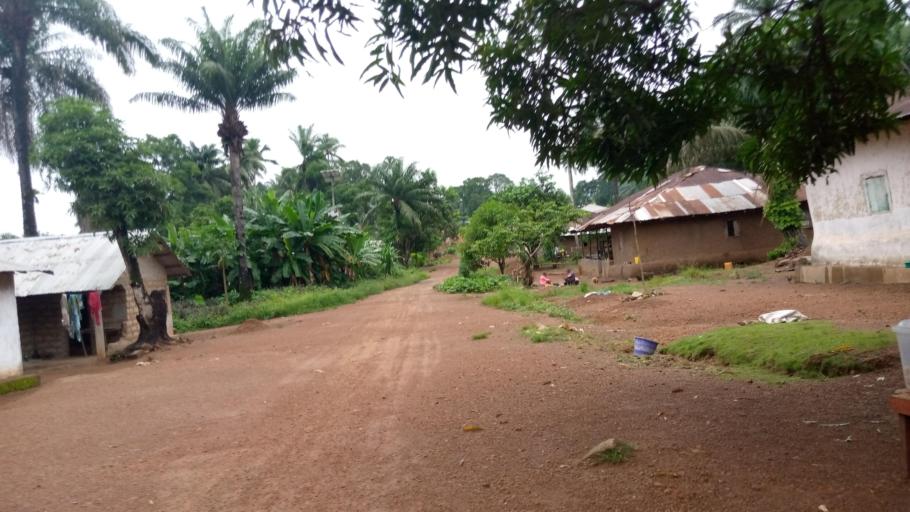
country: SL
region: Southern Province
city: Moyamba
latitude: 8.1630
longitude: -12.4302
